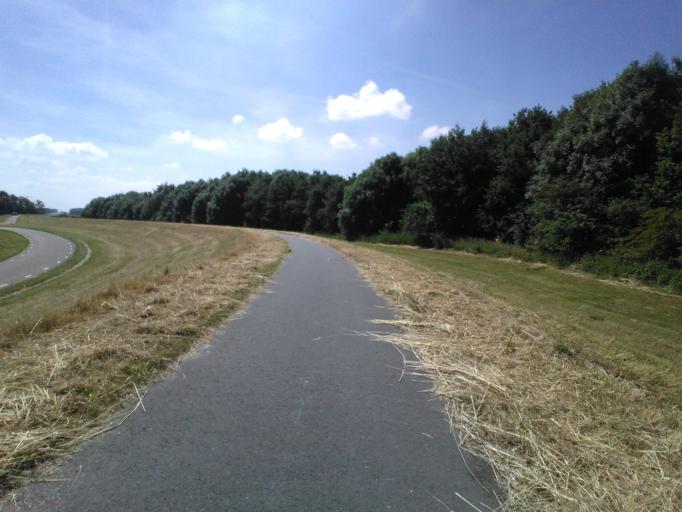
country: NL
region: North Brabant
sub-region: Gemeente Geertruidenberg
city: Geertruidenberg
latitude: 51.7467
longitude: 4.8526
